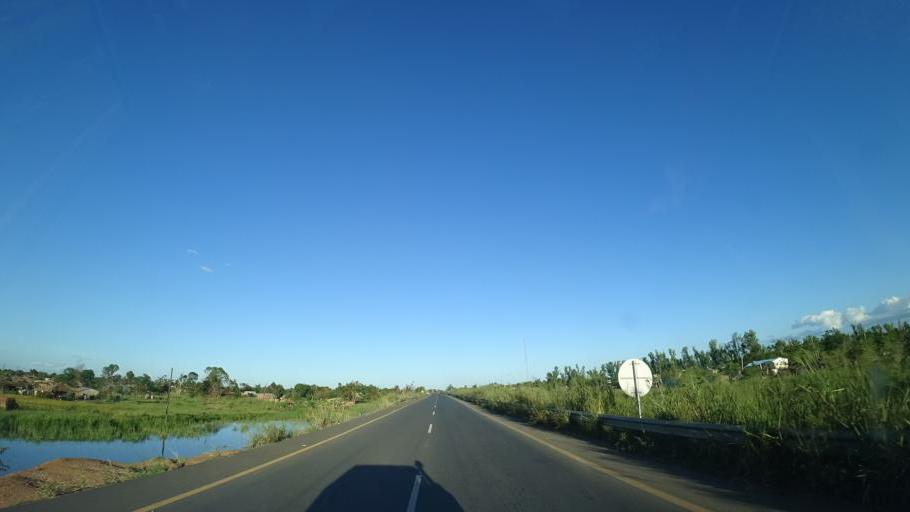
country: MZ
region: Sofala
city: Dondo
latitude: -19.3296
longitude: 34.3121
